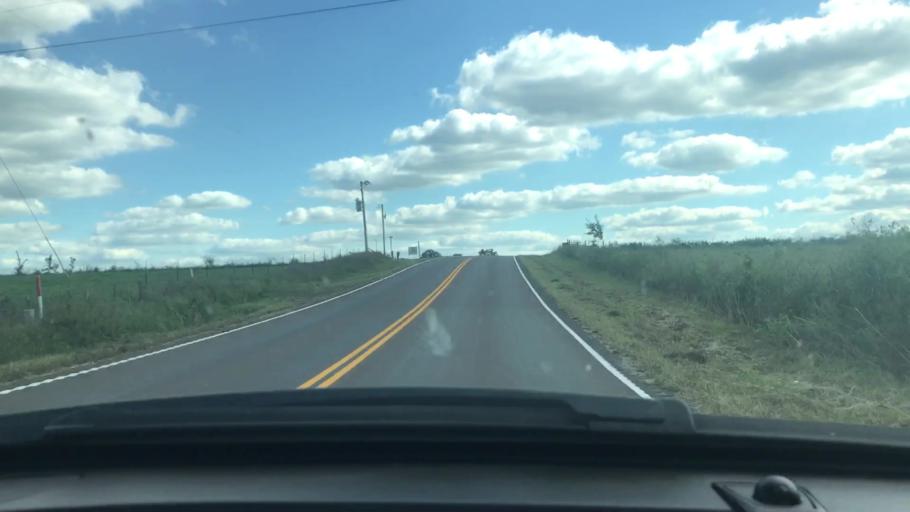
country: US
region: Missouri
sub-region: Wright County
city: Mountain Grove
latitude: 37.2927
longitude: -92.3083
